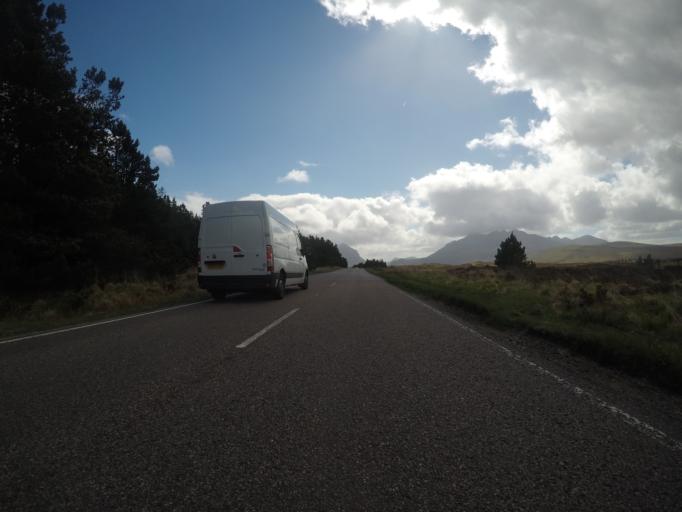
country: GB
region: Scotland
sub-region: Highland
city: Isle of Skye
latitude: 57.3171
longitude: -6.2018
